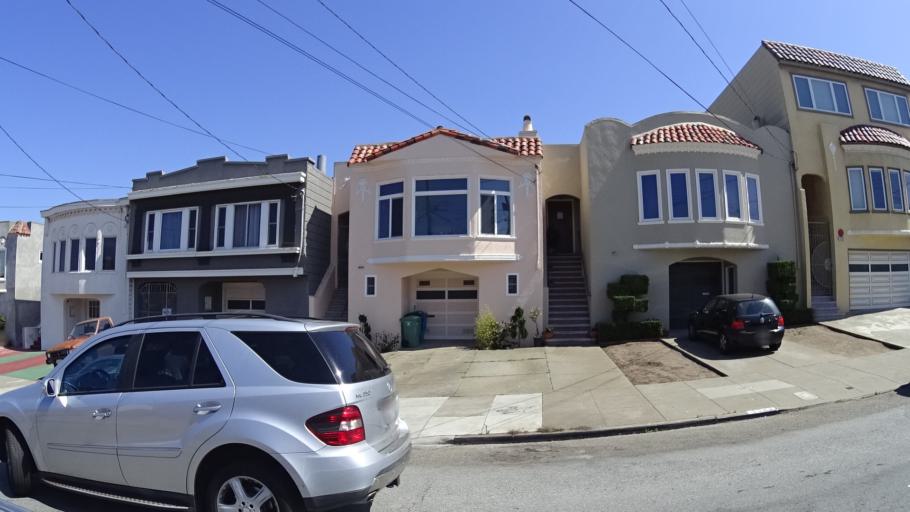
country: US
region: California
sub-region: San Mateo County
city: Daly City
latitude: 37.7626
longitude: -122.4803
